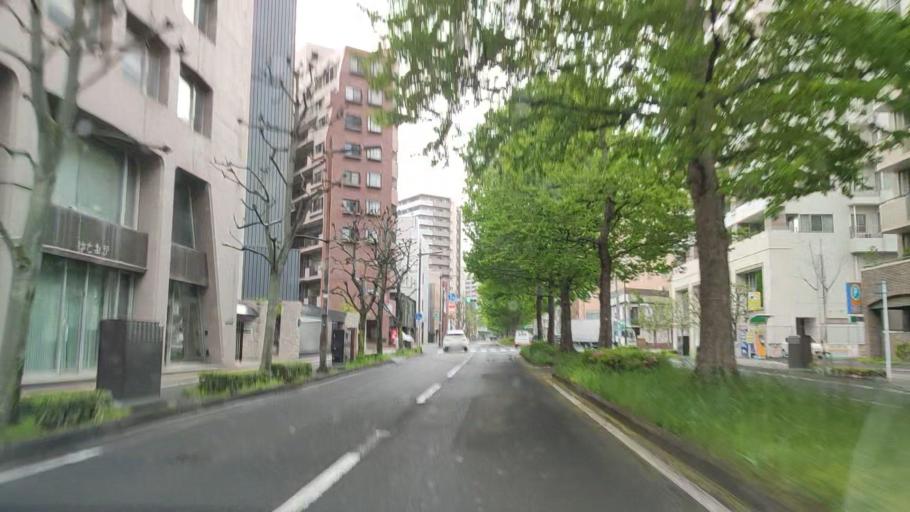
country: JP
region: Miyagi
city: Sendai
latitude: 38.2563
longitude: 140.8728
